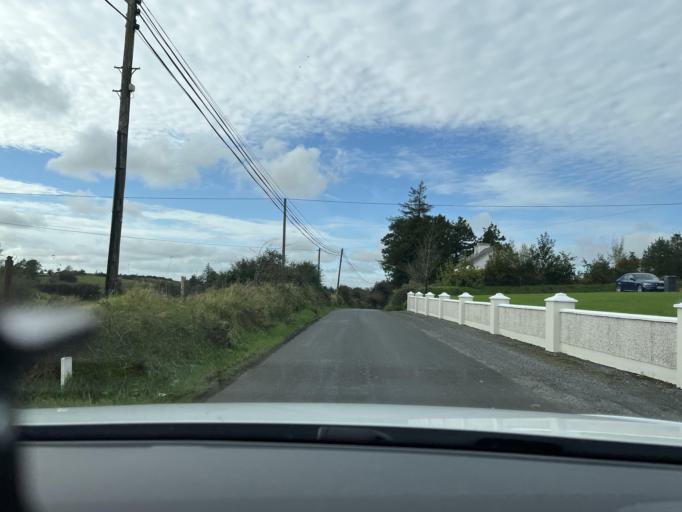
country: IE
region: Connaught
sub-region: Roscommon
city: Boyle
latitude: 54.0222
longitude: -8.3876
